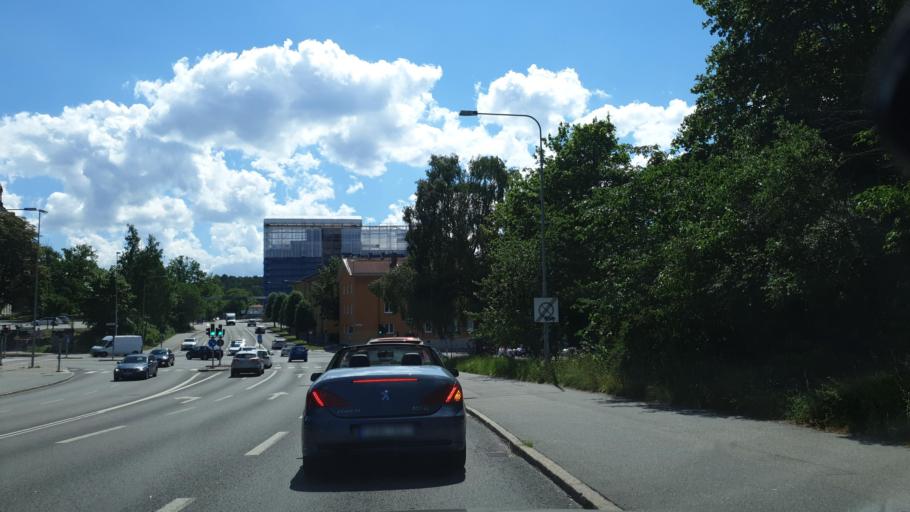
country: SE
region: Stockholm
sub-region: Sodertalje Kommun
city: Soedertaelje
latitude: 59.2016
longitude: 17.6323
